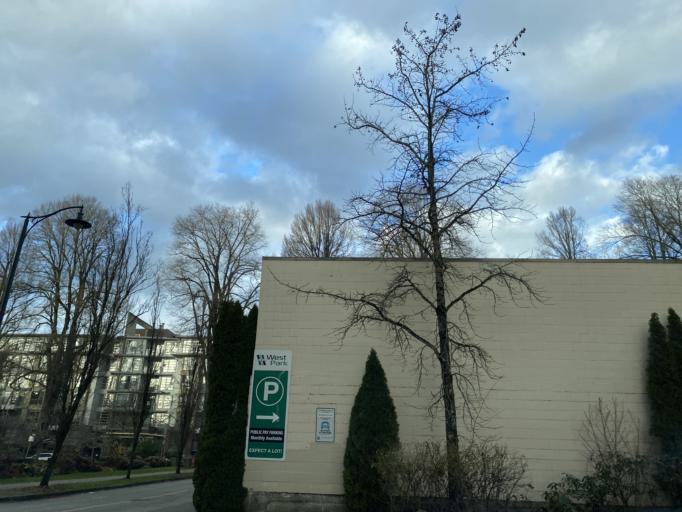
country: CA
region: British Columbia
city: West End
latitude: 49.2623
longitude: -123.1537
